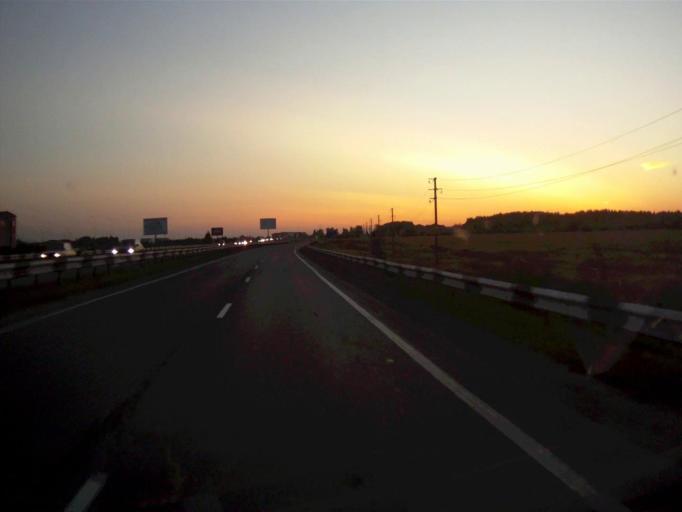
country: RU
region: Chelyabinsk
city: Roshchino
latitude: 55.1938
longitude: 61.1964
